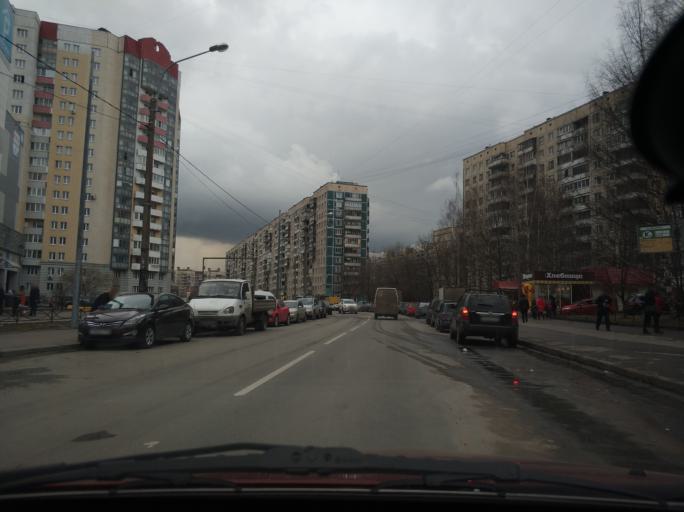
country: RU
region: St.-Petersburg
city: Krasnogvargeisky
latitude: 59.9456
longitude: 30.4844
